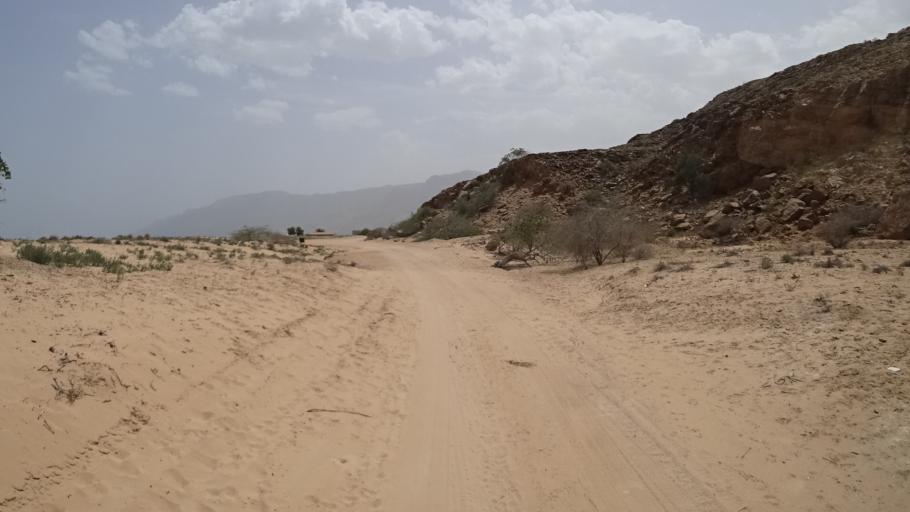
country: OM
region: Muhafazat Masqat
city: Muscat
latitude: 23.4434
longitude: 58.7796
